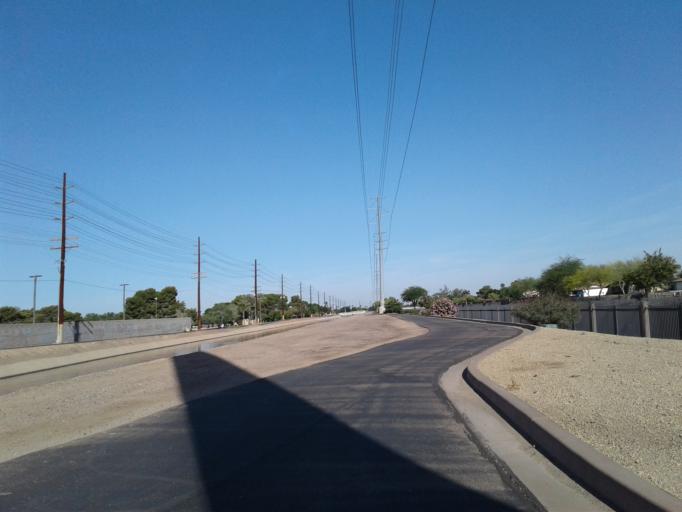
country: US
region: Arizona
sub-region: Maricopa County
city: Glendale
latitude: 33.5705
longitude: -112.1290
